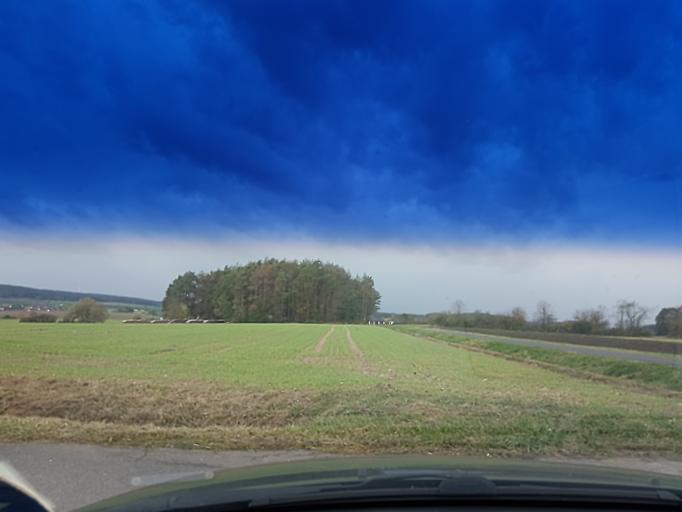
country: DE
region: Bavaria
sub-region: Regierungsbezirk Mittelfranken
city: Wachenroth
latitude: 49.7546
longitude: 10.6800
